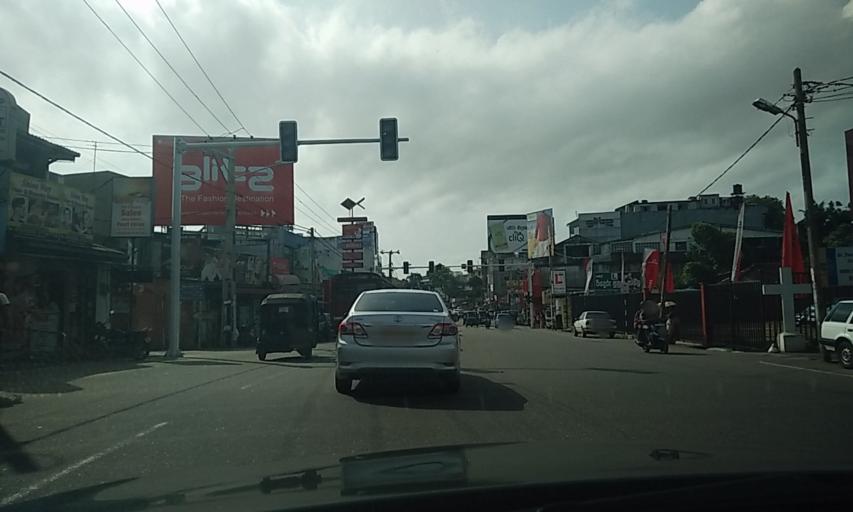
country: LK
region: Western
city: Sri Jayewardenepura Kotte
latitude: 6.8660
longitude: 79.8937
